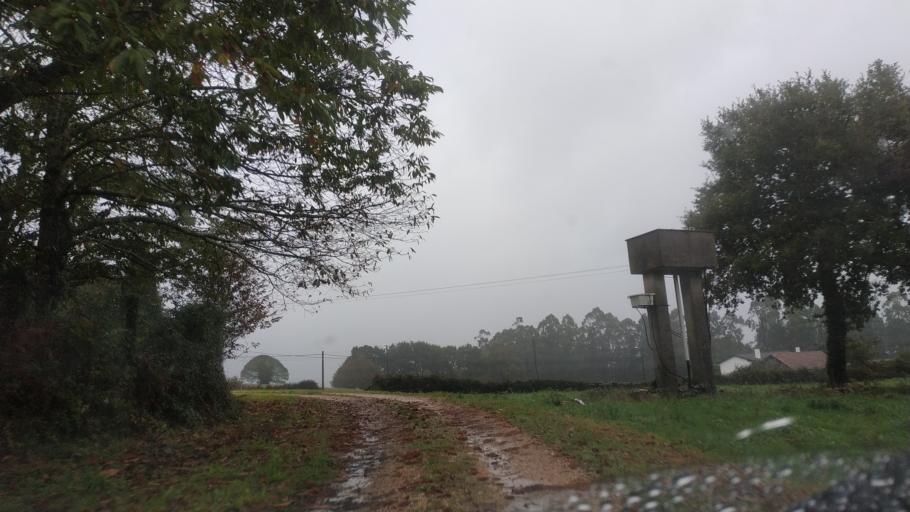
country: ES
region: Galicia
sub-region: Provincia da Coruna
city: Negreira
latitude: 42.9095
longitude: -8.7626
